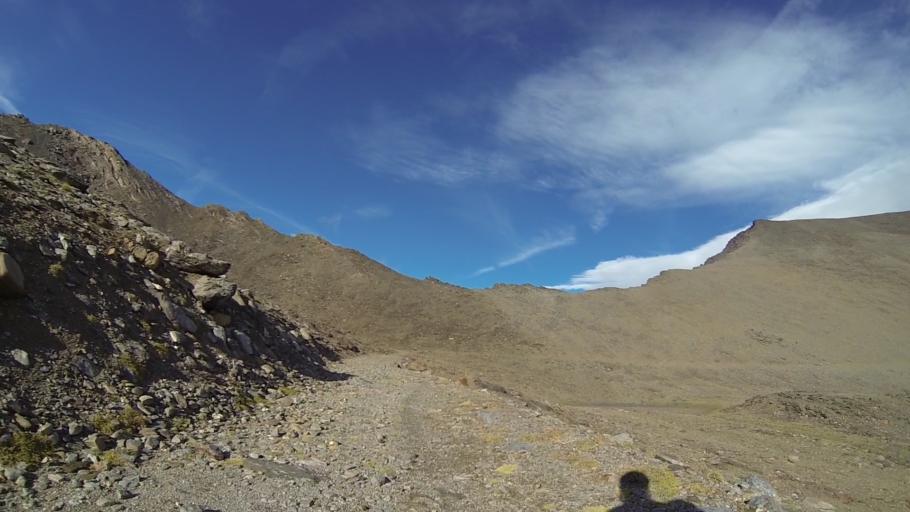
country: ES
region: Andalusia
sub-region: Provincia de Granada
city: Trevelez
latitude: 37.0533
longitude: -3.3257
